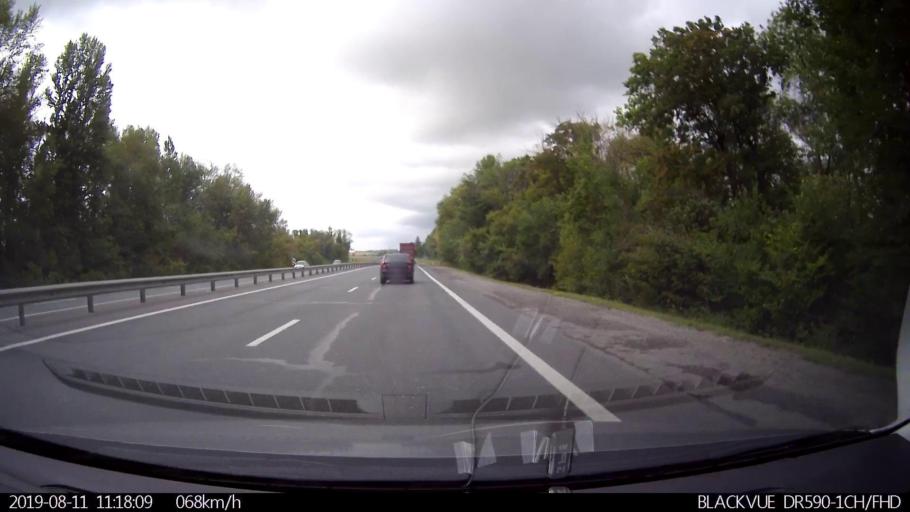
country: RU
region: Ulyanovsk
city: Novoul'yanovsk
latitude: 54.1826
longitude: 48.2709
